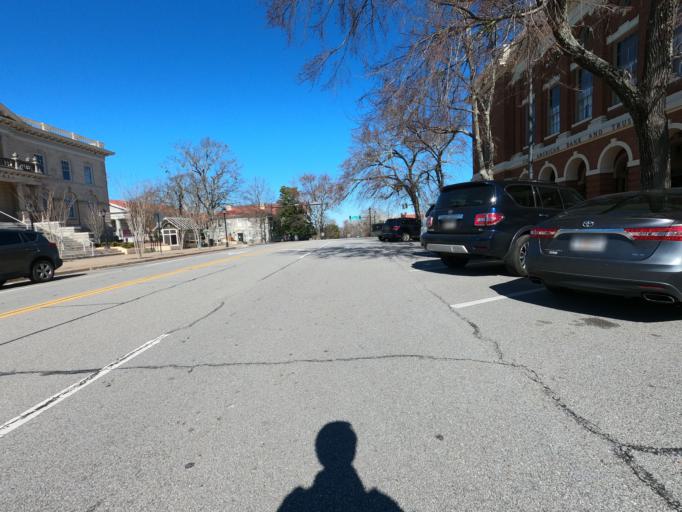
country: US
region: Georgia
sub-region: Clarke County
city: Athens
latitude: 33.9596
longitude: -83.3759
